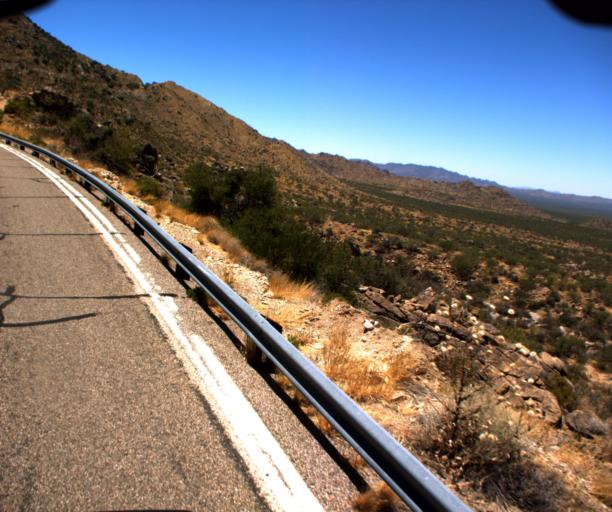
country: US
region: Arizona
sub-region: Pima County
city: Three Points
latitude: 31.9914
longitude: -111.5860
